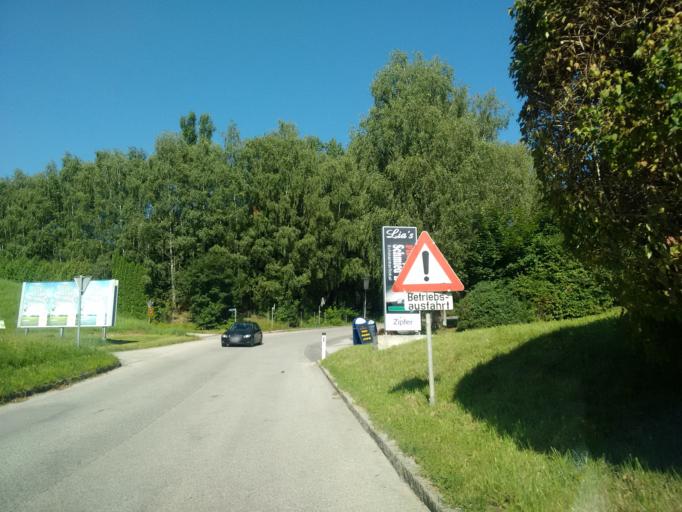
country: AT
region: Upper Austria
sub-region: Politischer Bezirk Steyr-Land
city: Pfarrkirchen bei Bad Hall
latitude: 48.0247
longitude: 14.2059
